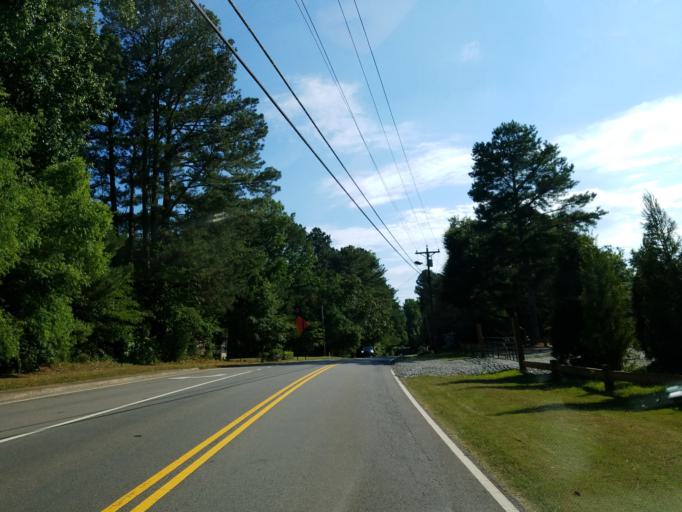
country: US
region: Georgia
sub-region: Fulton County
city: Milton
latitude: 34.1718
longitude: -84.3287
